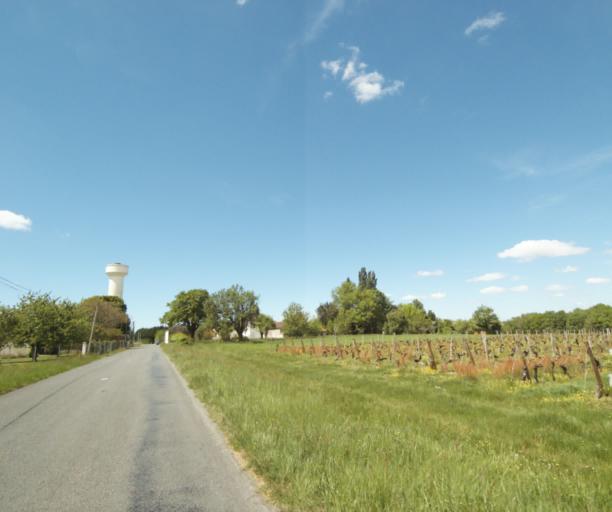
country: FR
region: Poitou-Charentes
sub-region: Departement de la Charente-Maritime
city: Burie
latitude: 45.7609
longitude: -0.4728
